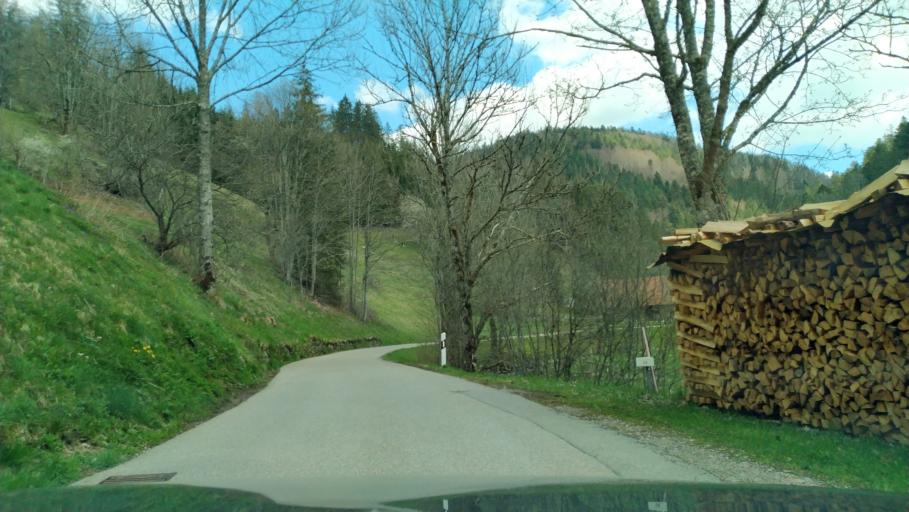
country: DE
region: Baden-Wuerttemberg
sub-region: Freiburg Region
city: Gutenbach
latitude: 48.0123
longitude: 8.1434
